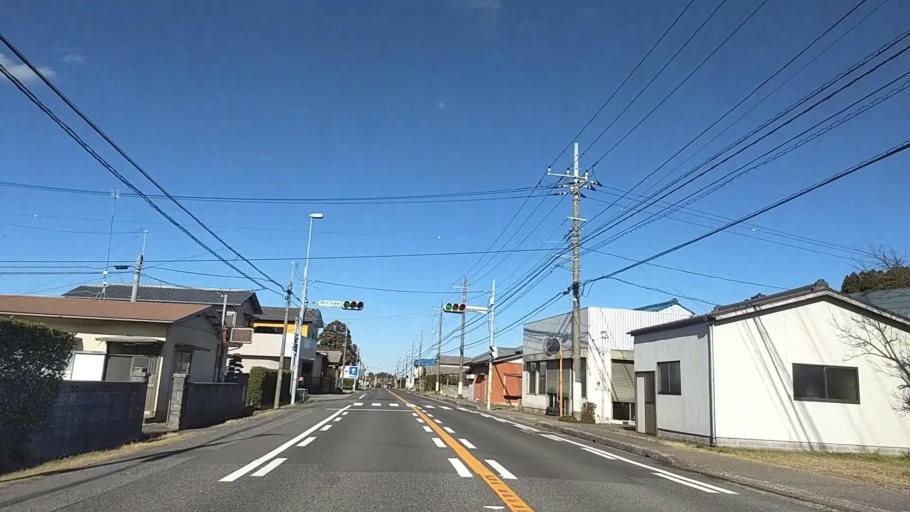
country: JP
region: Chiba
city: Ohara
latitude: 35.2296
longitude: 140.3876
